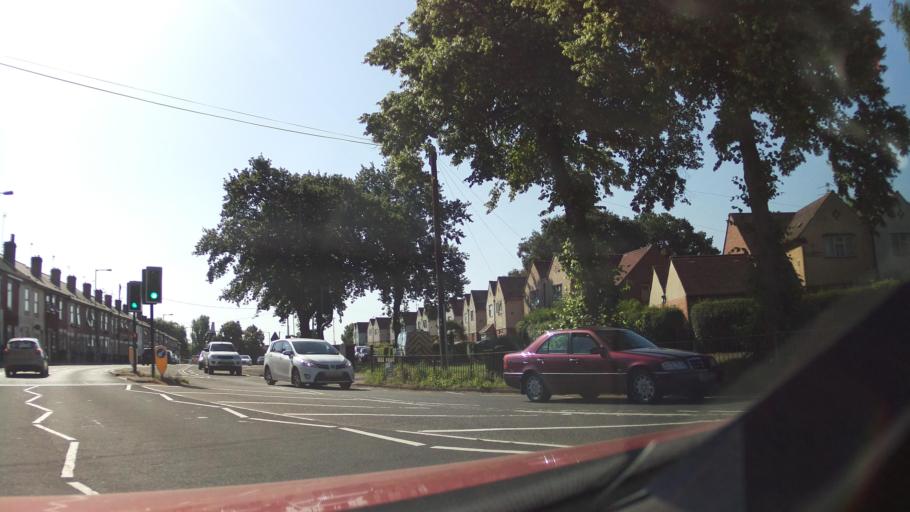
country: GB
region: England
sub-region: Derby
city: Derby
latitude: 52.8986
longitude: -1.4814
